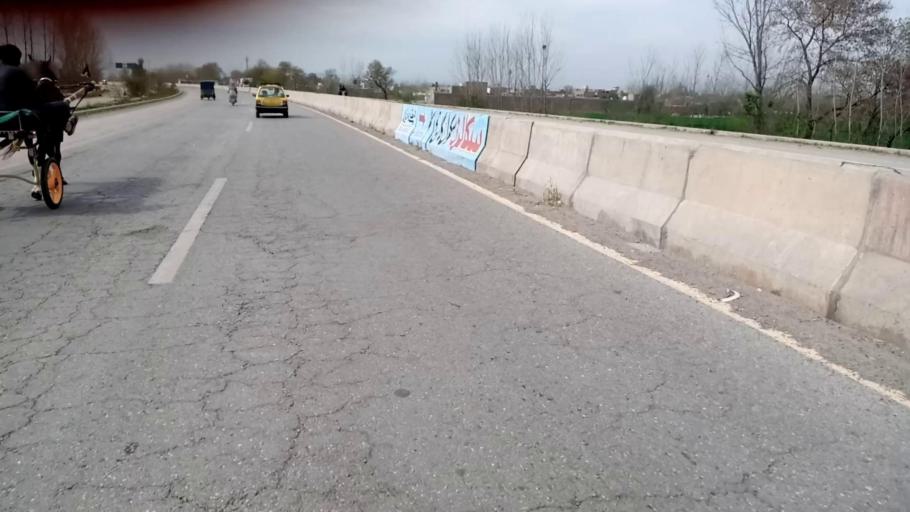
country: PK
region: Khyber Pakhtunkhwa
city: Peshawar
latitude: 34.0658
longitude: 71.5995
